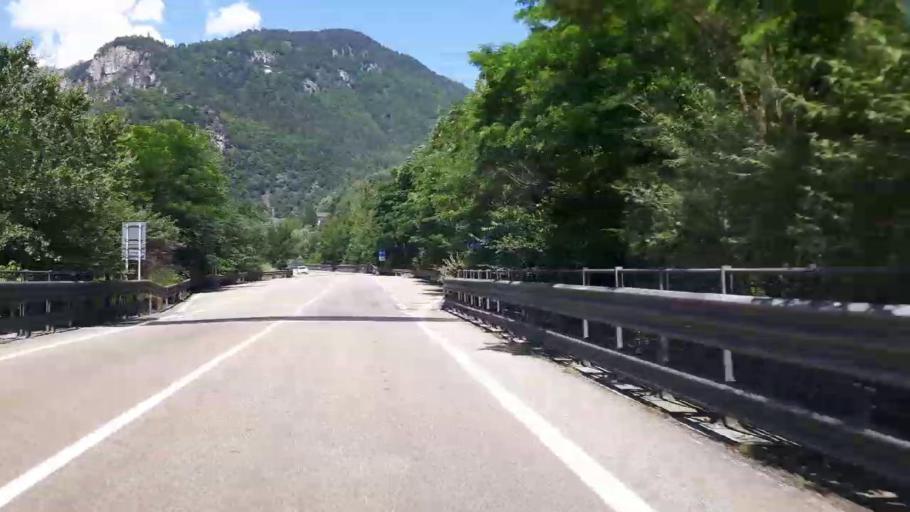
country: IT
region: Piedmont
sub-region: Provincia Verbano-Cusio-Ossola
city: Varzo
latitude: 46.2051
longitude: 8.2465
